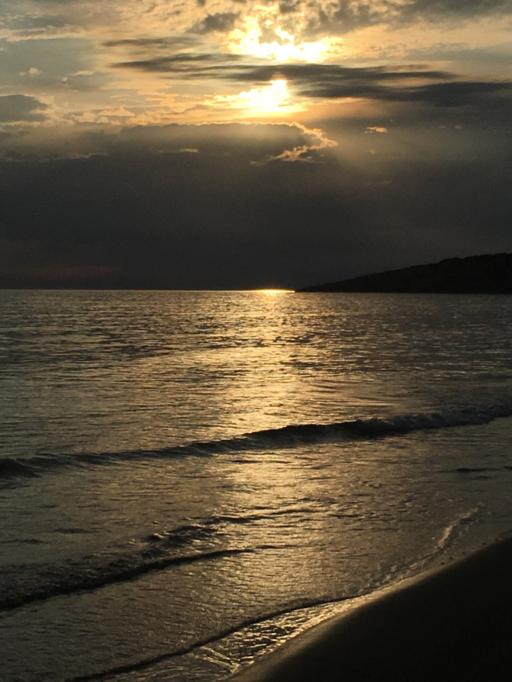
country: ME
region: Ulcinj
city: Ulcinj
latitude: 41.9053
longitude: 19.2548
